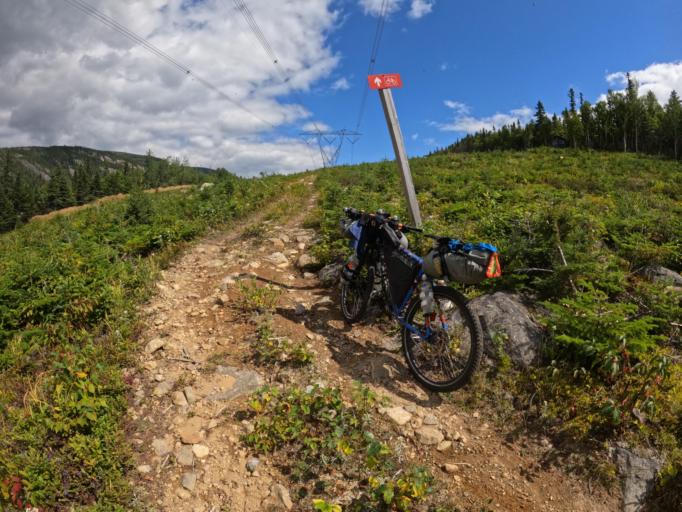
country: CA
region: Quebec
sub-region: Capitale-Nationale
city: La Malbaie
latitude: 47.8960
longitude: -70.3749
